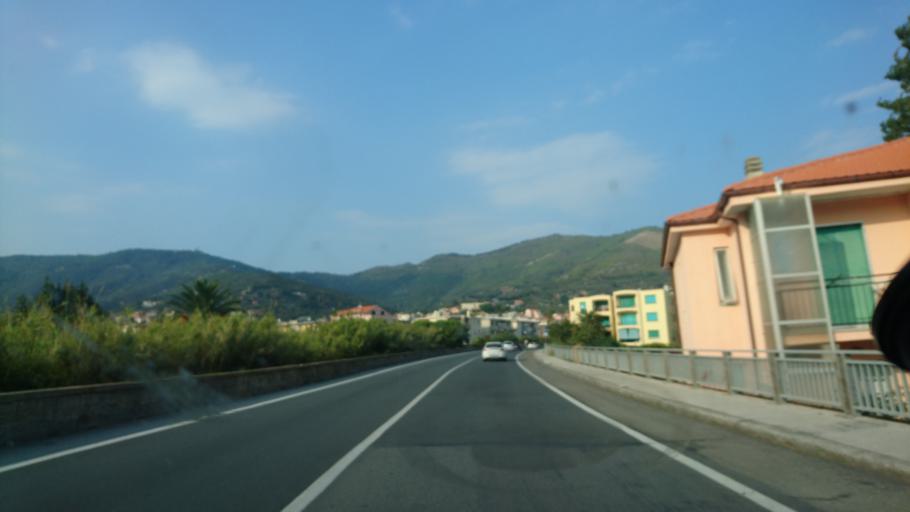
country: IT
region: Liguria
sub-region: Provincia di Savona
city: Spotorno
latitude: 44.2231
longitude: 8.4143
